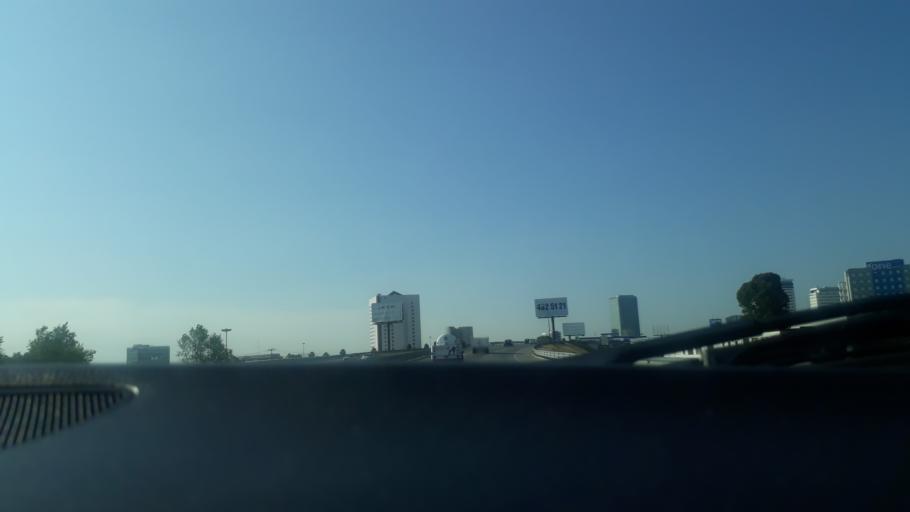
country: MX
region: Puebla
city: Tlazcalancingo
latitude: 19.0110
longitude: -98.2623
